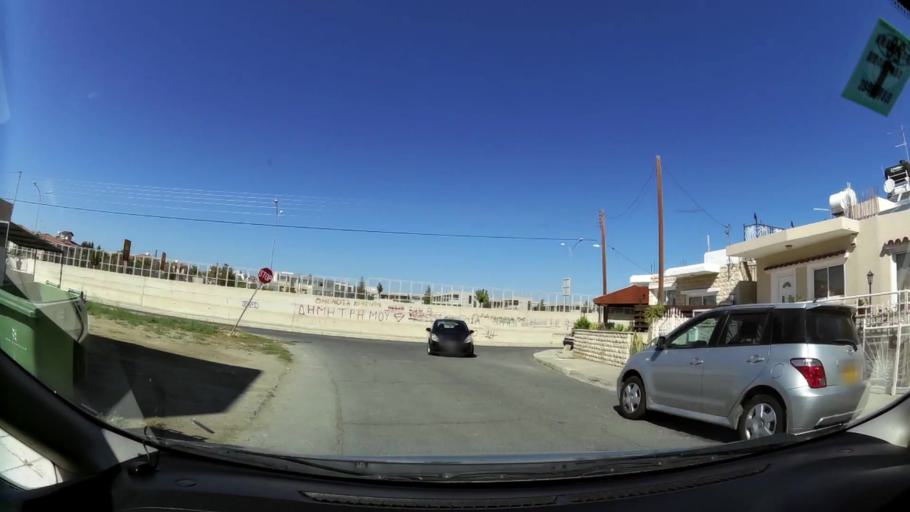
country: CY
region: Larnaka
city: Livadia
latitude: 34.9371
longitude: 33.6300
